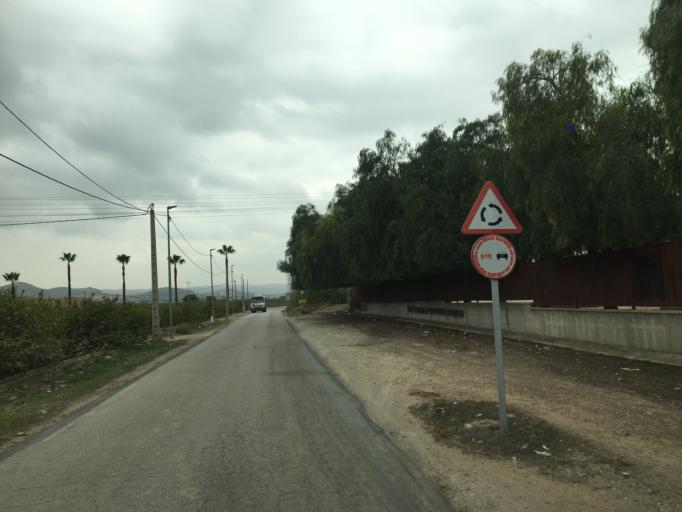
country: ES
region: Murcia
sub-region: Murcia
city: Santomera
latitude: 38.0810
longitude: -1.0550
